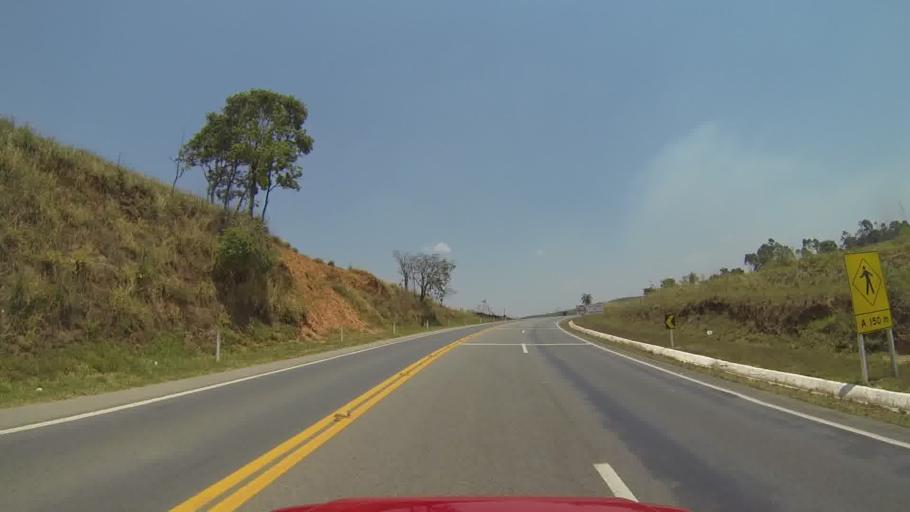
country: BR
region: Minas Gerais
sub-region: Itapecerica
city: Itapecerica
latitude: -20.3440
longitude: -45.2453
